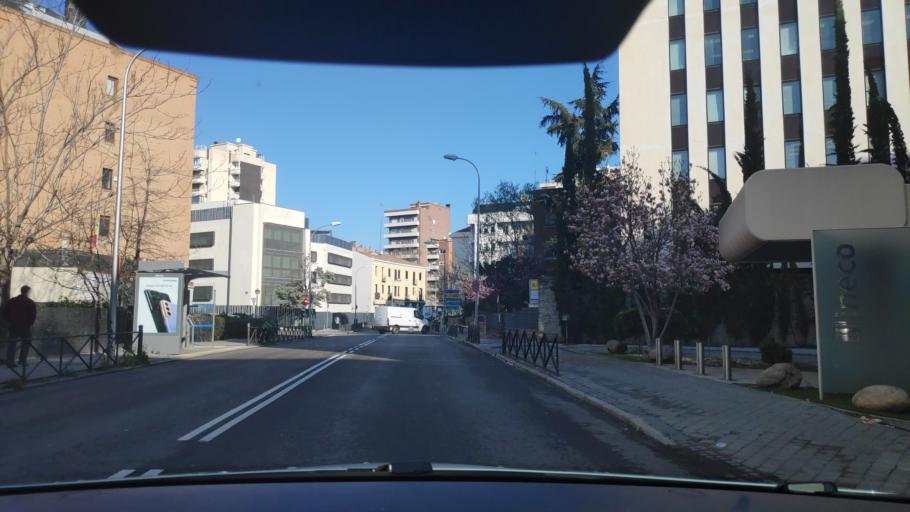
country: ES
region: Madrid
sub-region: Provincia de Madrid
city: Chamartin
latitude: 40.4573
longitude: -3.6813
